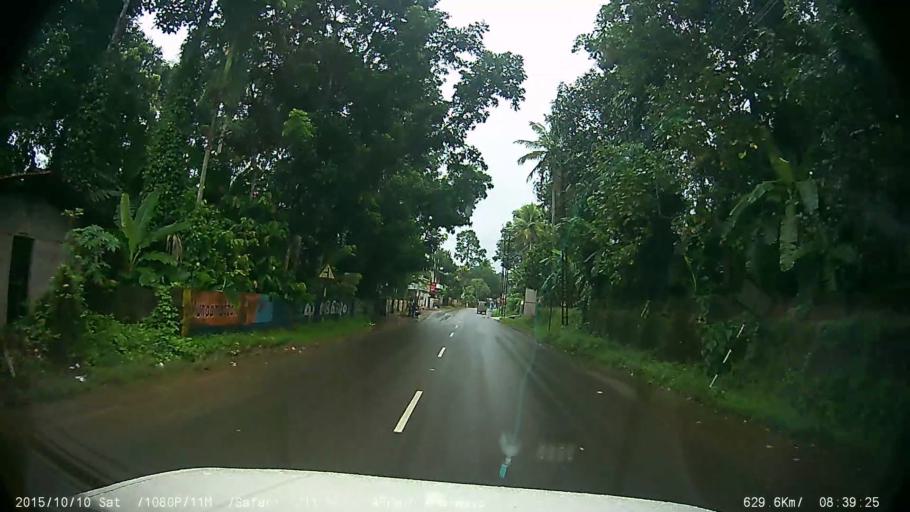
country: IN
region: Kerala
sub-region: Kottayam
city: Palackattumala
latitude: 9.7564
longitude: 76.5580
